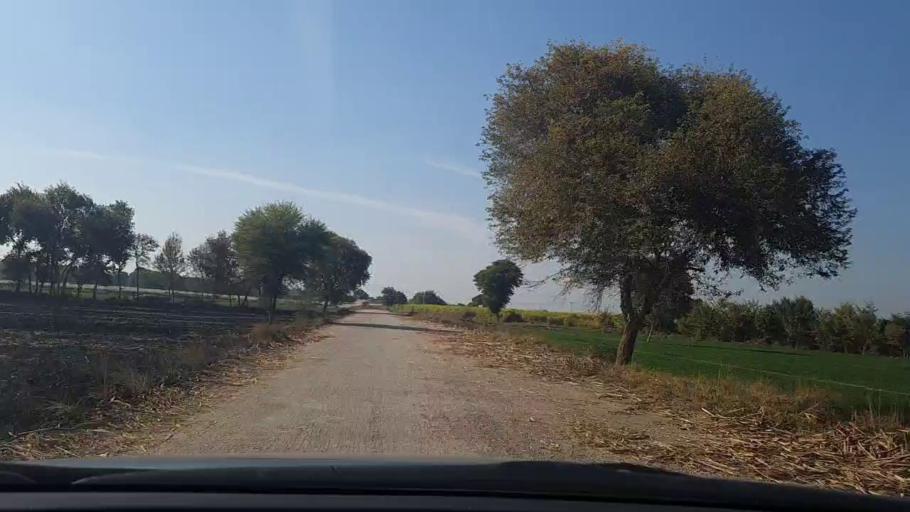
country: PK
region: Sindh
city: Sehwan
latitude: 26.3358
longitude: 67.9800
